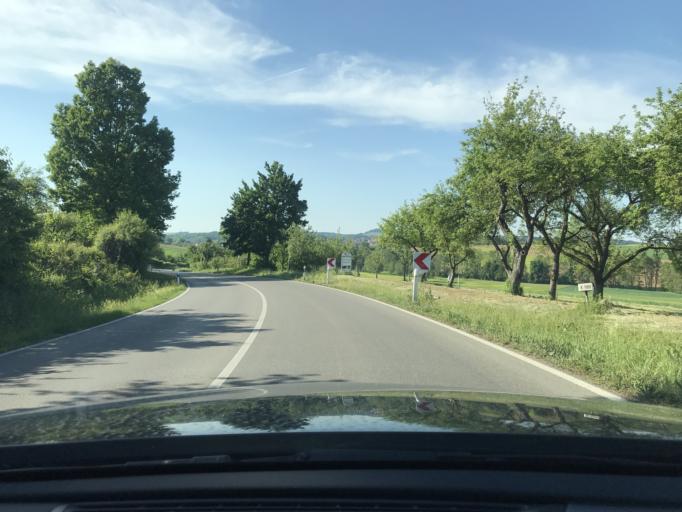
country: DE
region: Baden-Wuerttemberg
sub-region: Regierungsbezirk Stuttgart
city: Schwaikheim
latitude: 48.8765
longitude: 9.3199
